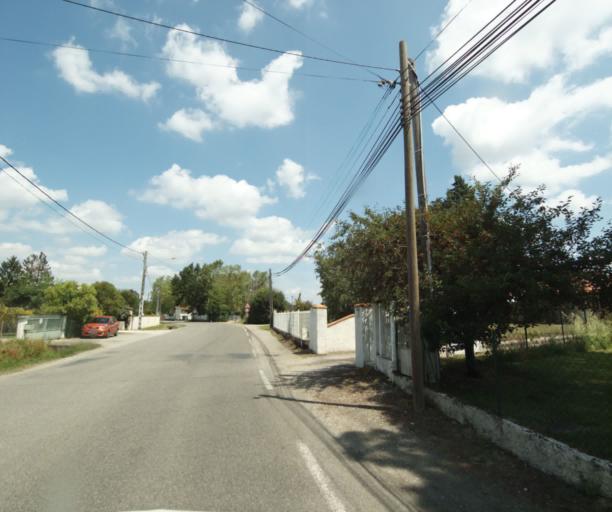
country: FR
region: Midi-Pyrenees
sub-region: Departement du Tarn-et-Garonne
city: Montauban
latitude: 44.0604
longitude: 1.3359
